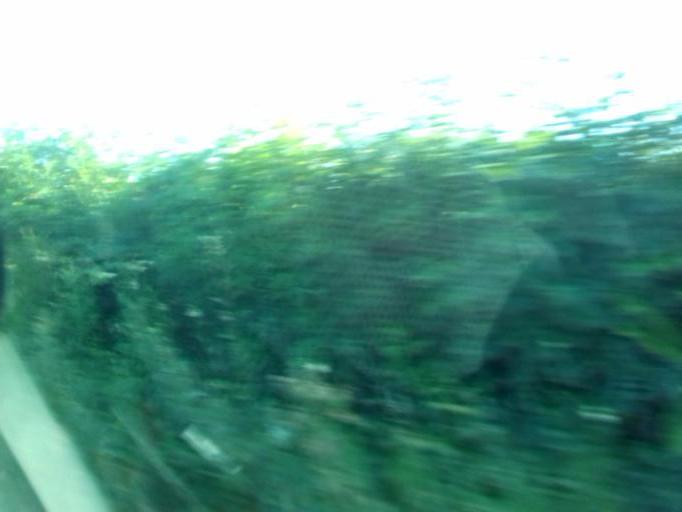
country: IE
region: Leinster
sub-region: Fingal County
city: Swords
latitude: 53.4964
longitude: -6.2844
